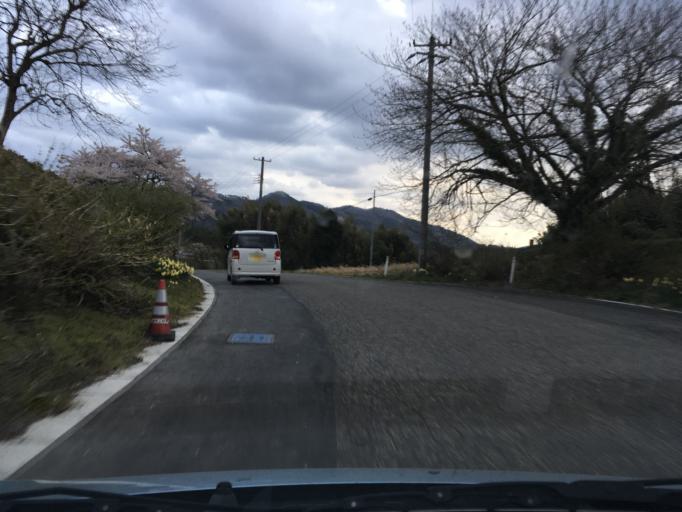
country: JP
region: Iwate
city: Ichinoseki
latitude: 38.9708
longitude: 141.2131
